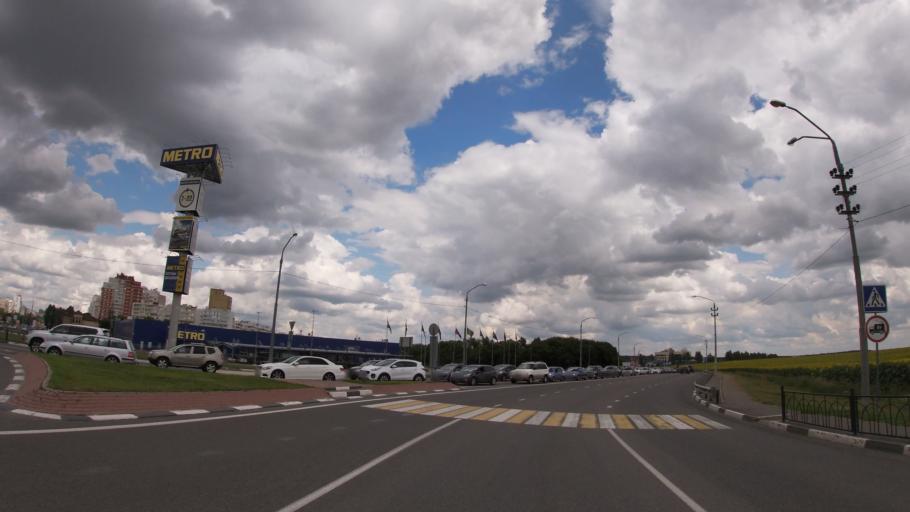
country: RU
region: Belgorod
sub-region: Belgorodskiy Rayon
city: Belgorod
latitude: 50.5512
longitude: 36.5736
